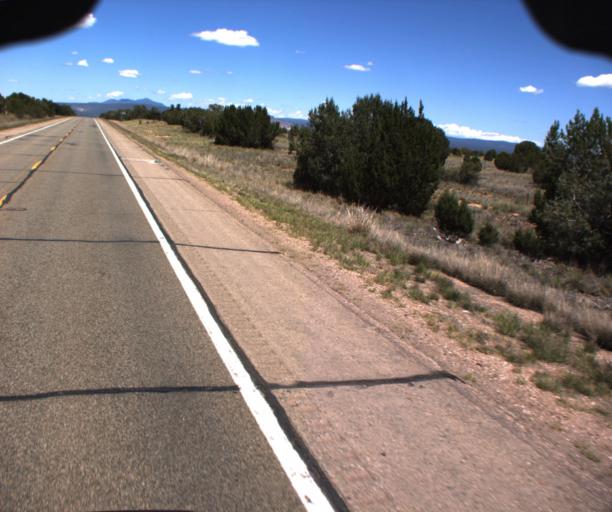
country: US
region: Arizona
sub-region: Yavapai County
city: Paulden
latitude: 34.9445
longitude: -112.4265
